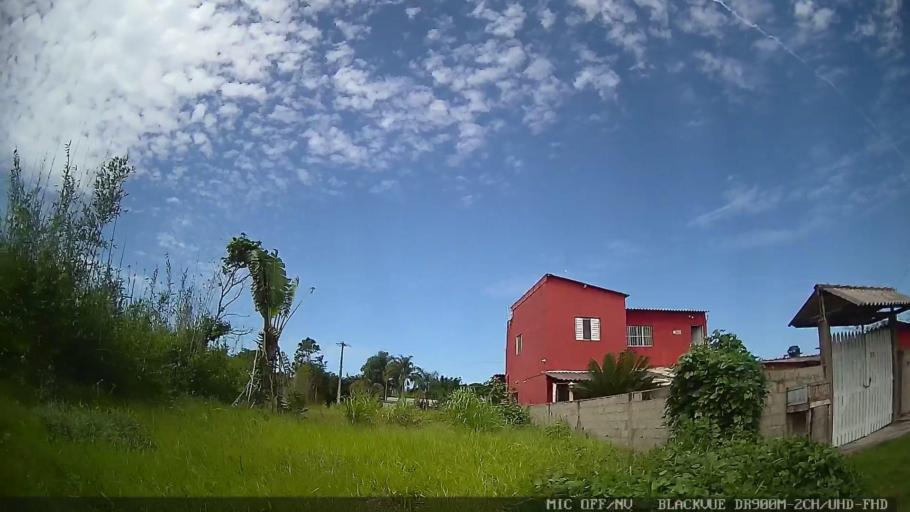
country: BR
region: Sao Paulo
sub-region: Iguape
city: Iguape
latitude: -24.7212
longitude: -47.5297
